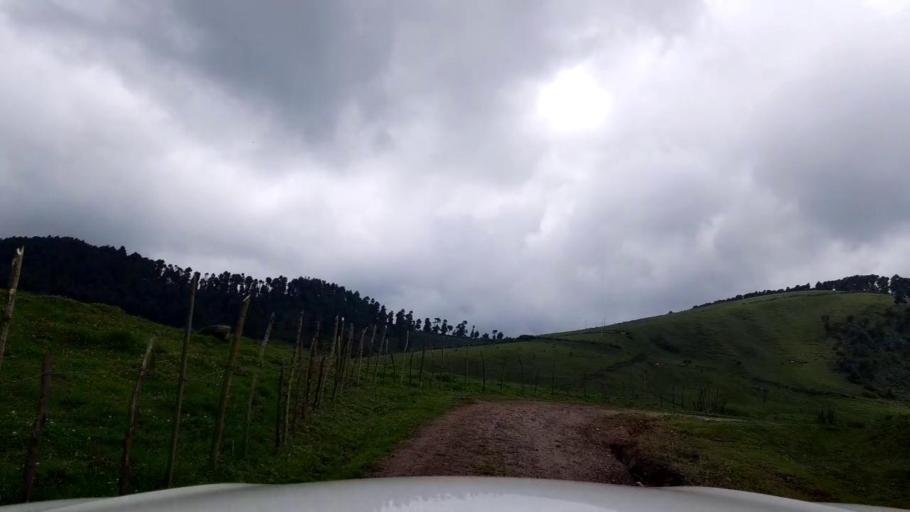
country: RW
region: Western Province
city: Gisenyi
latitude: -1.6897
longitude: 29.4258
